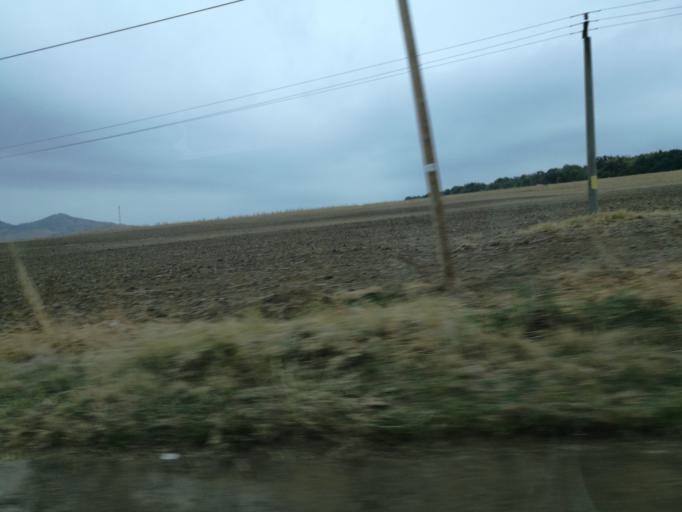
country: RO
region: Tulcea
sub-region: Comuna Horia
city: Horia
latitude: 45.0201
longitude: 28.4474
